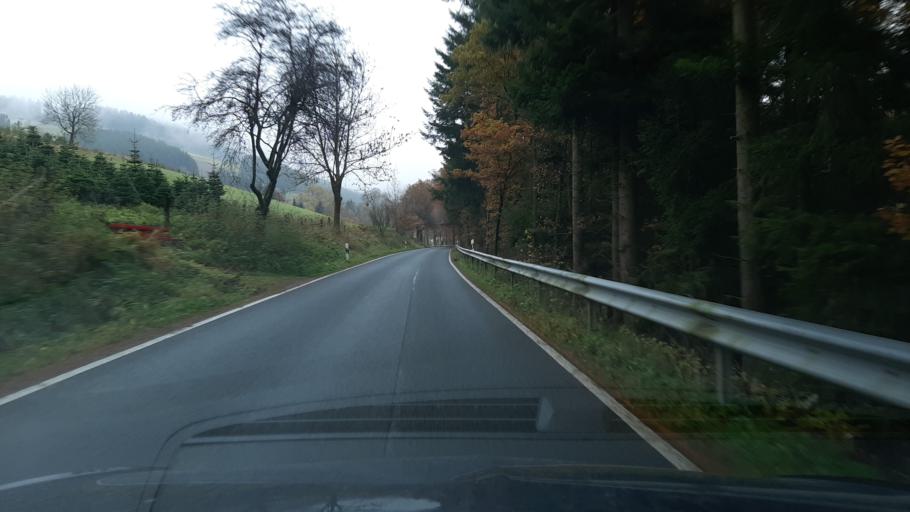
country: DE
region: North Rhine-Westphalia
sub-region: Regierungsbezirk Arnsberg
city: Bad Fredeburg
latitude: 51.1955
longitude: 8.3900
